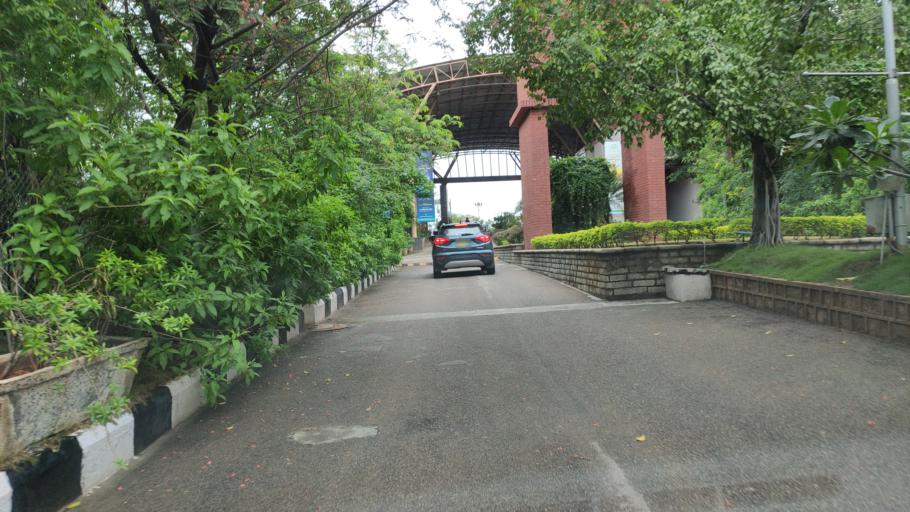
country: IN
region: Telangana
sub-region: Rangareddi
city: Secunderabad
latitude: 17.5784
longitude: 78.6016
